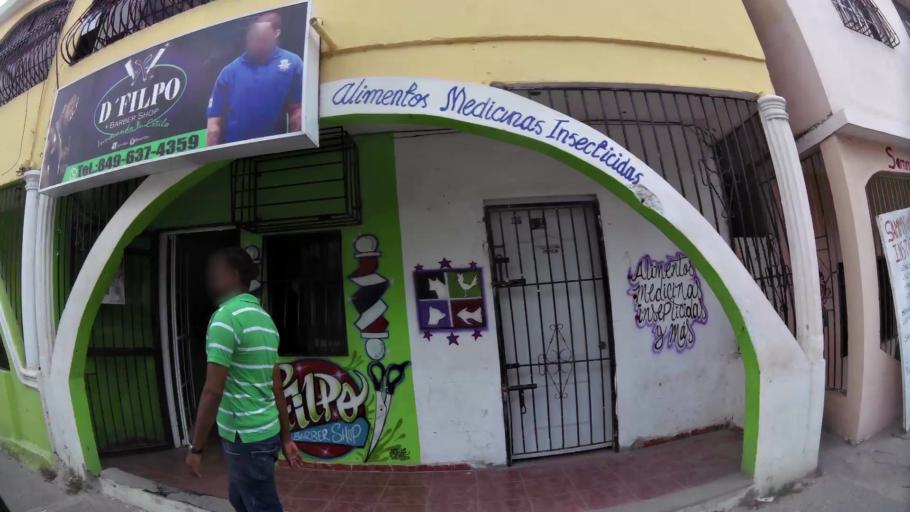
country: DO
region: San Cristobal
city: San Cristobal
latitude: 18.4078
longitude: -70.1135
